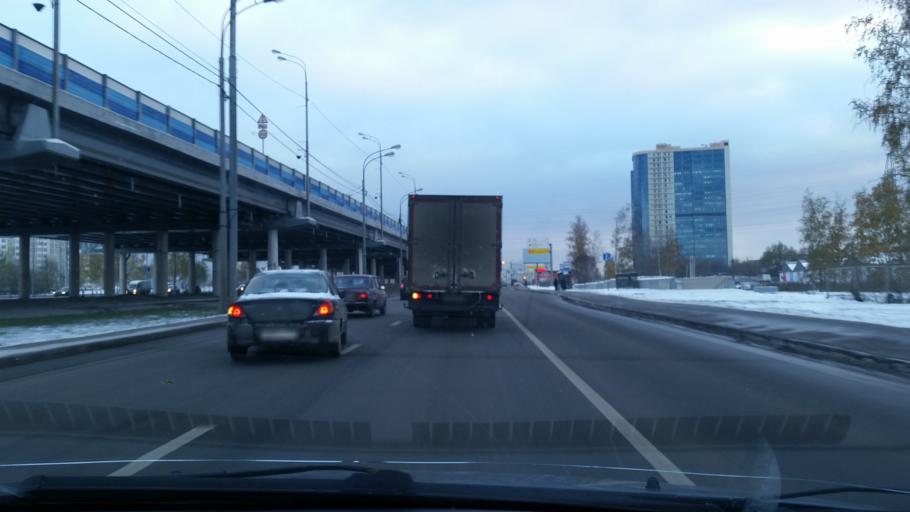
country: RU
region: Moscow
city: Vagonoremont
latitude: 55.9161
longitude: 37.5437
